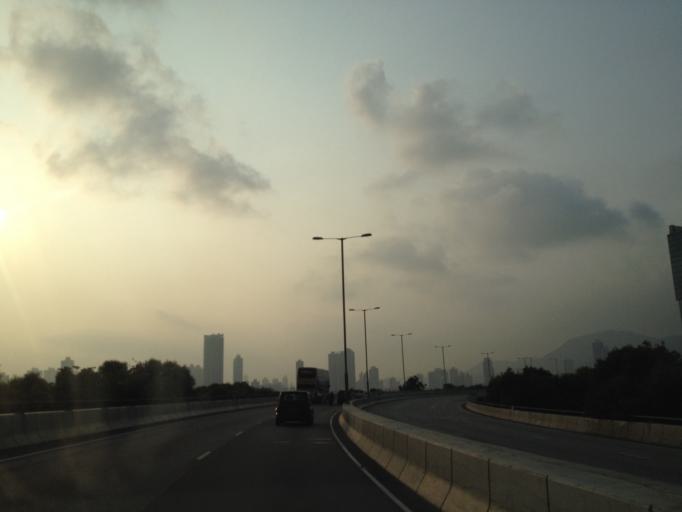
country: HK
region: Kowloon City
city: Kowloon
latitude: 22.3171
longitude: 114.2102
